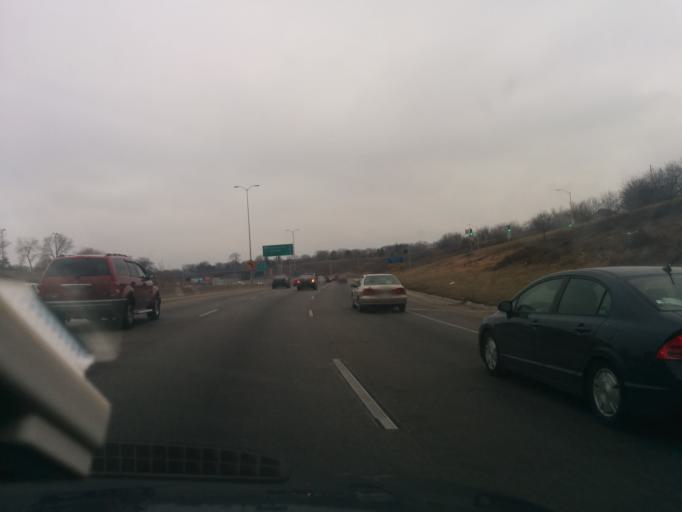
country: US
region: Wisconsin
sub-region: Milwaukee County
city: Milwaukee
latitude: 43.0598
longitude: -87.9216
